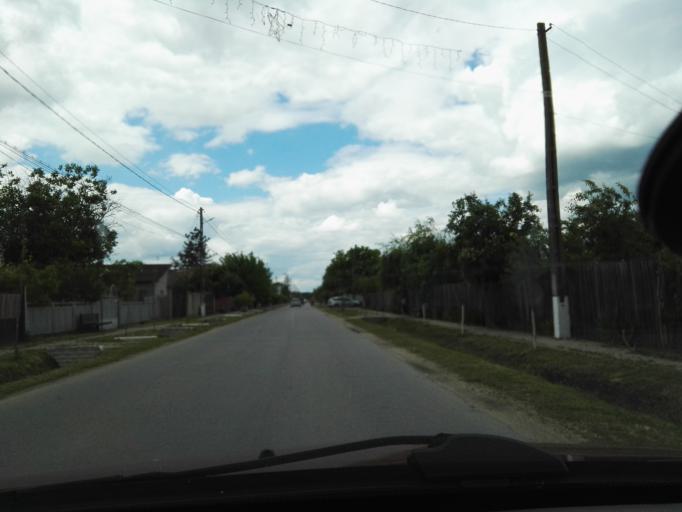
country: RO
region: Giurgiu
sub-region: Comuna Comana
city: Gradistea
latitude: 44.2124
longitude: 26.1569
